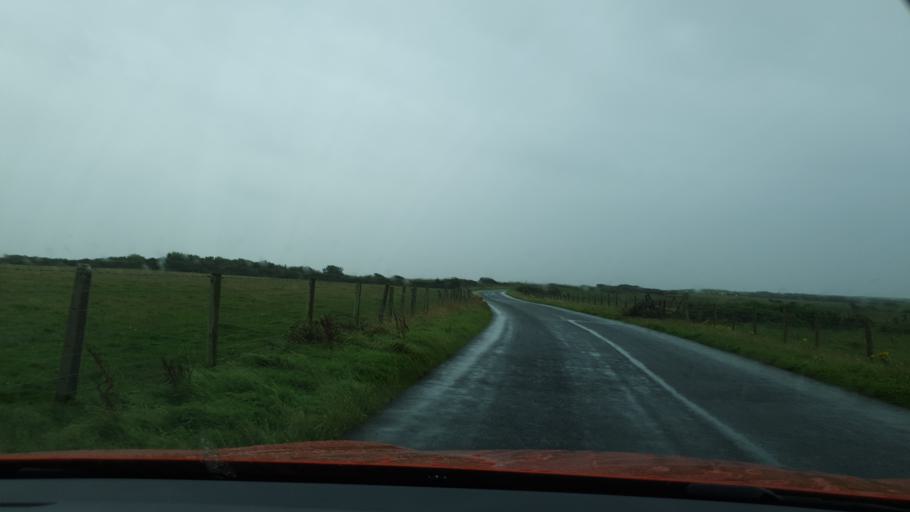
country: GB
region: England
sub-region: Cumbria
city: Barrow in Furness
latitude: 54.0796
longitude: -3.2317
